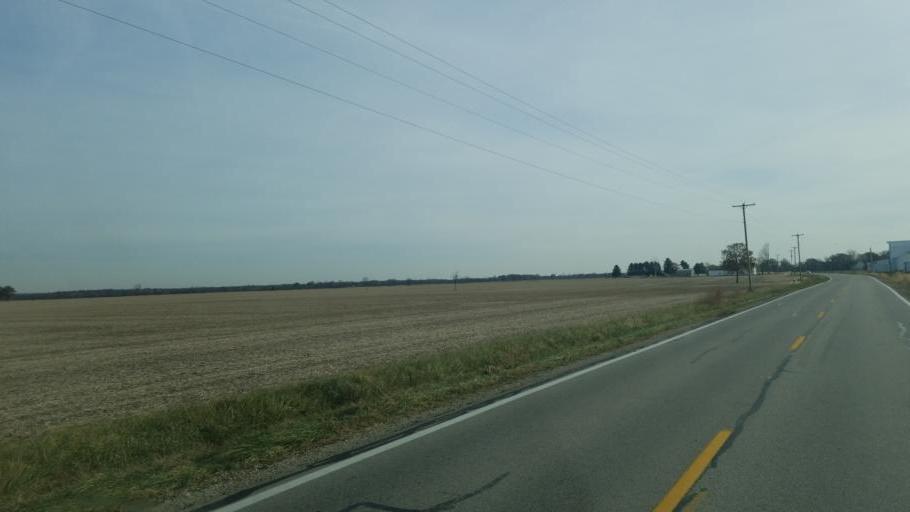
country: US
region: Ohio
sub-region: Madison County
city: Plain City
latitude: 40.1143
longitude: -83.3368
